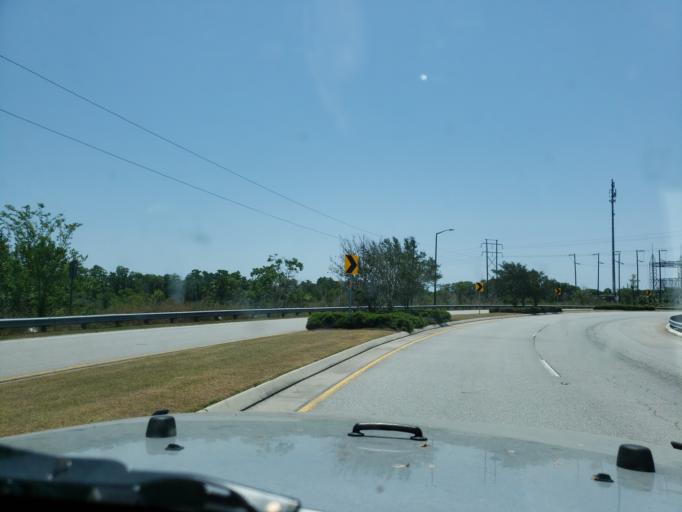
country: US
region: Georgia
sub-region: Chatham County
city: Savannah
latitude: 32.0965
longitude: -81.0907
